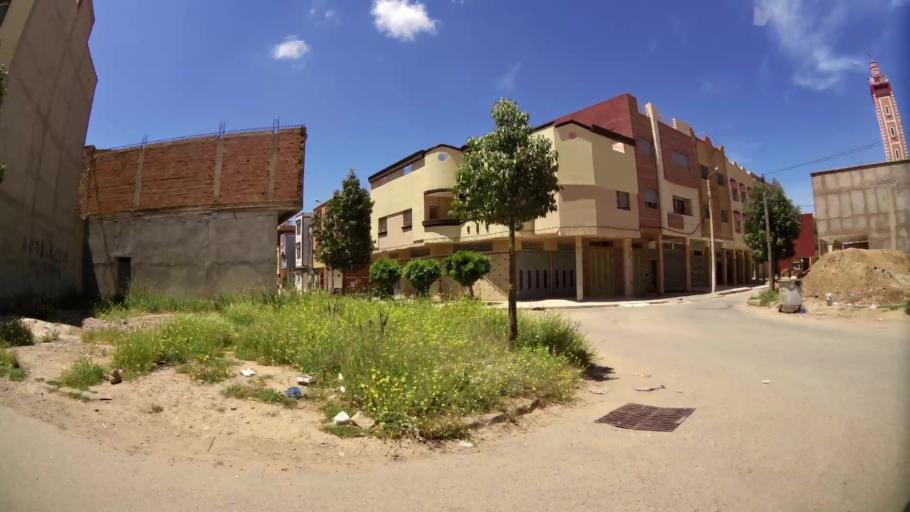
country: MA
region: Oriental
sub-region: Oujda-Angad
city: Oujda
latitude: 34.6648
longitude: -1.9404
